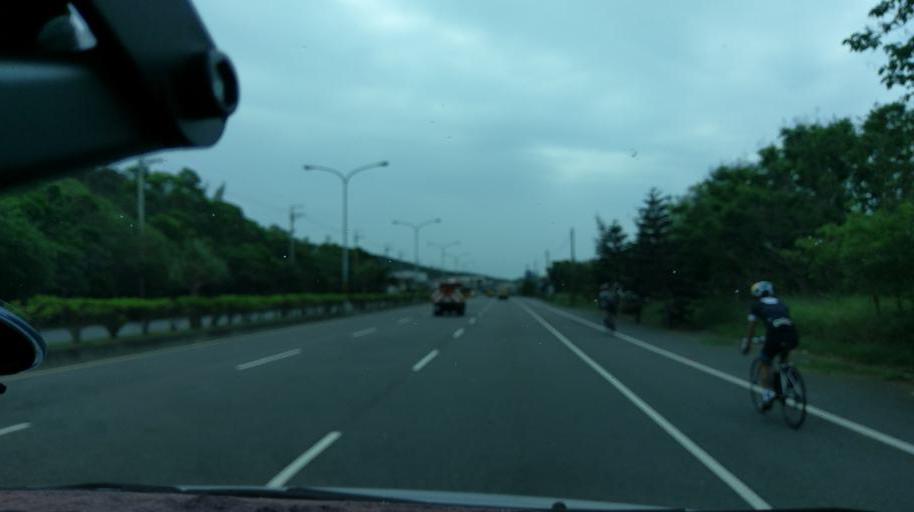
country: TW
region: Taiwan
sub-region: Miaoli
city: Miaoli
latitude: 24.5195
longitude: 120.6919
